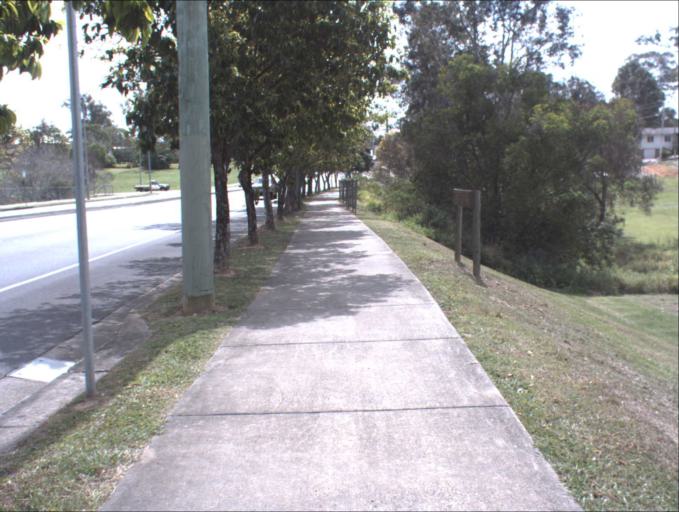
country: AU
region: Queensland
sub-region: Logan
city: Waterford West
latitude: -27.6744
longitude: 153.1385
